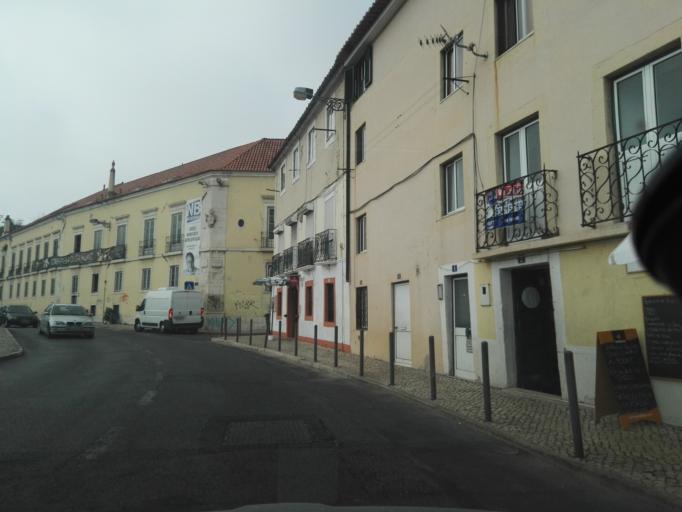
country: PT
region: Lisbon
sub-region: Lisbon
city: Lisbon
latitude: 38.7197
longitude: -9.1179
